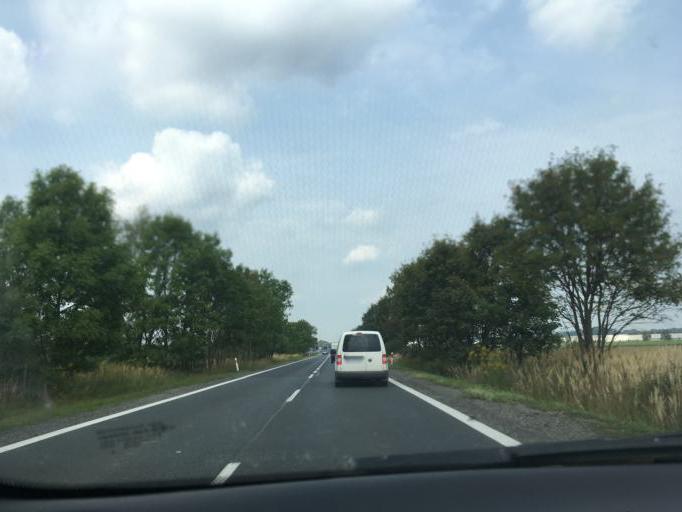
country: PL
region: Silesian Voivodeship
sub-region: Powiat bierunsko-ledzinski
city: Bierun
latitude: 50.0885
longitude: 19.1081
